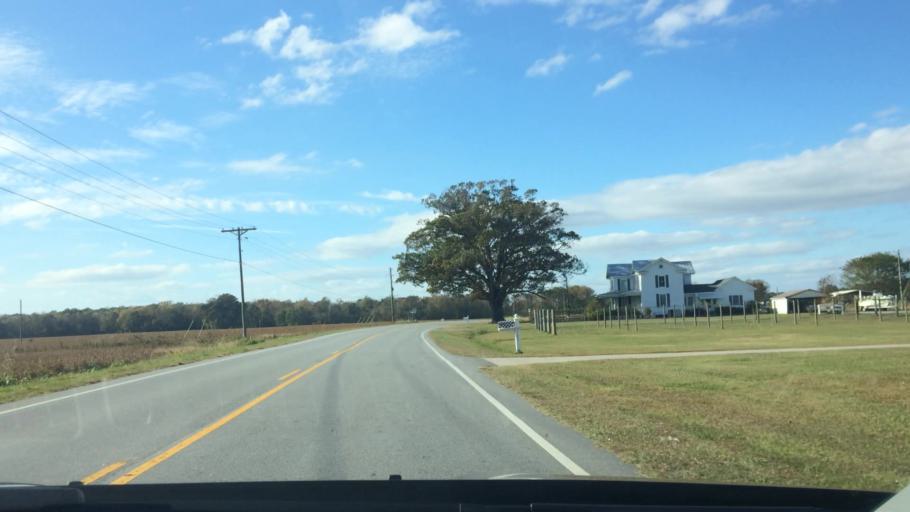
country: US
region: North Carolina
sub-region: Greene County
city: Maury
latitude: 35.4754
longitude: -77.5565
